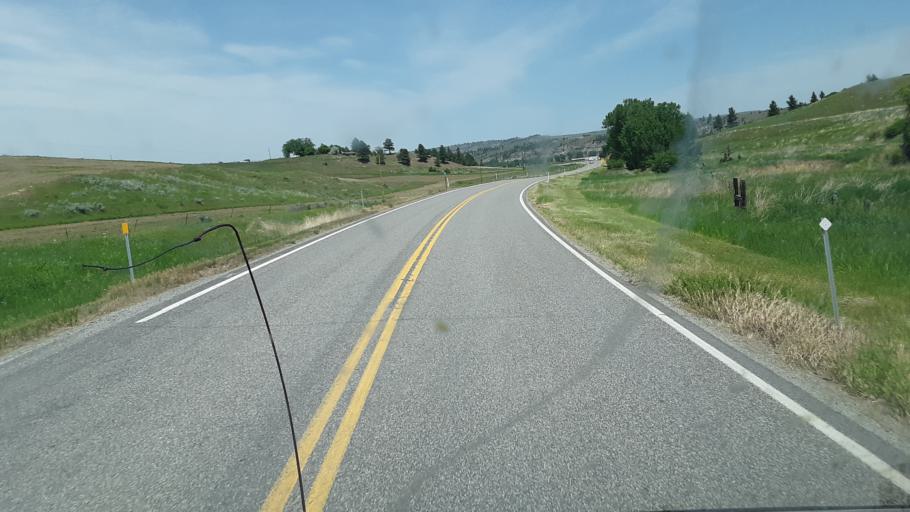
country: US
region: Montana
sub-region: Stillwater County
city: Columbus
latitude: 45.5984
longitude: -109.1990
